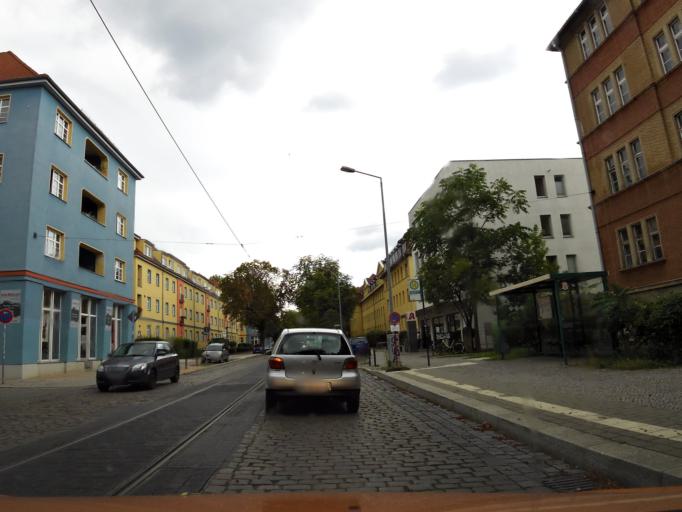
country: DE
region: Brandenburg
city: Potsdam
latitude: 52.3897
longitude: 13.0282
